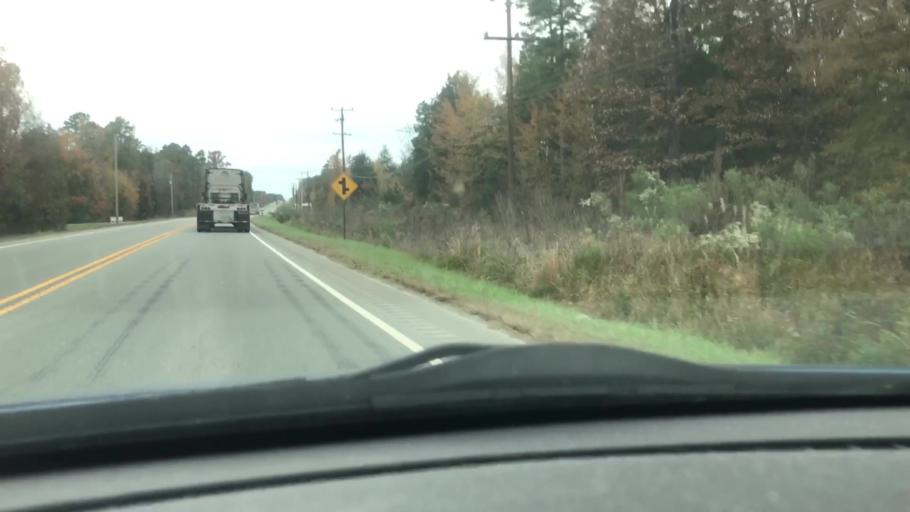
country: US
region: North Carolina
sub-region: Davidson County
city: Thomasville
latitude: 35.7786
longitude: -80.1193
